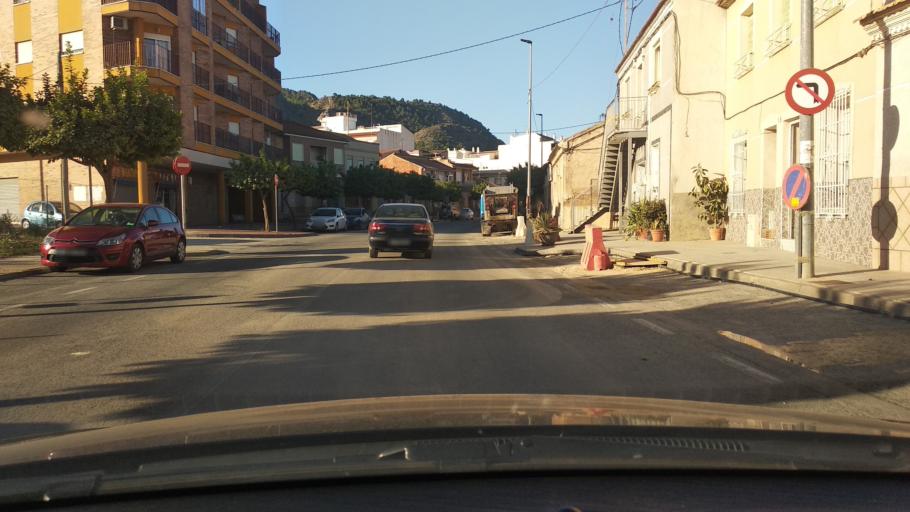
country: ES
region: Murcia
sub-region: Murcia
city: Beniel
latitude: 37.9943
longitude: -1.0332
